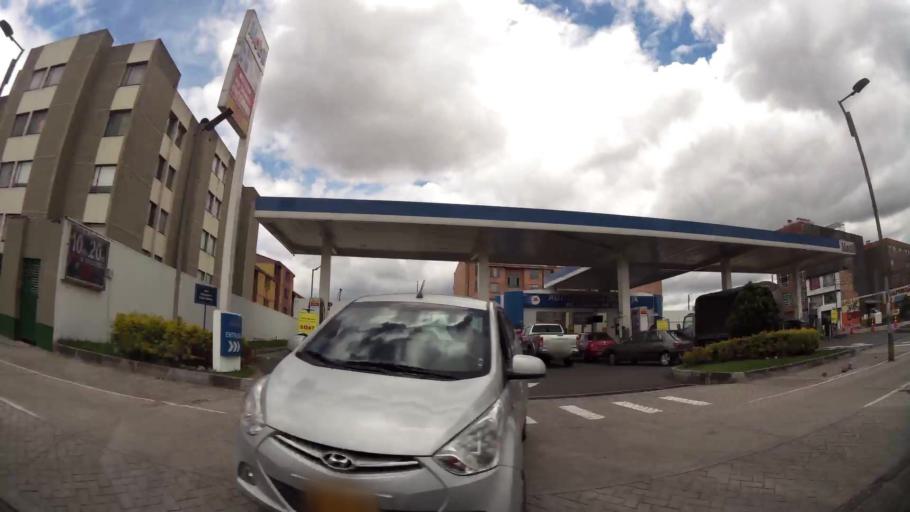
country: CO
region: Bogota D.C.
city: Barrio San Luis
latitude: 4.7085
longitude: -74.0960
